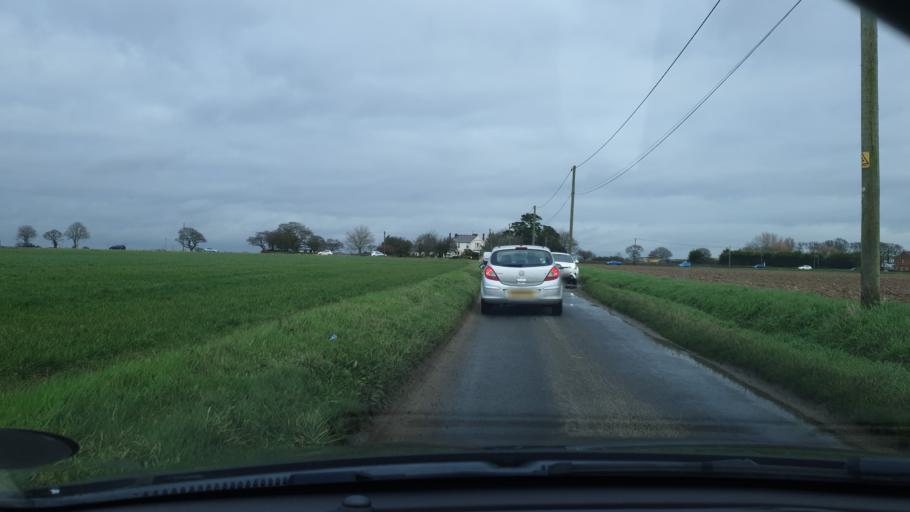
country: GB
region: England
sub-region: Essex
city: Frinton-on-Sea
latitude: 51.8452
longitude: 1.1936
